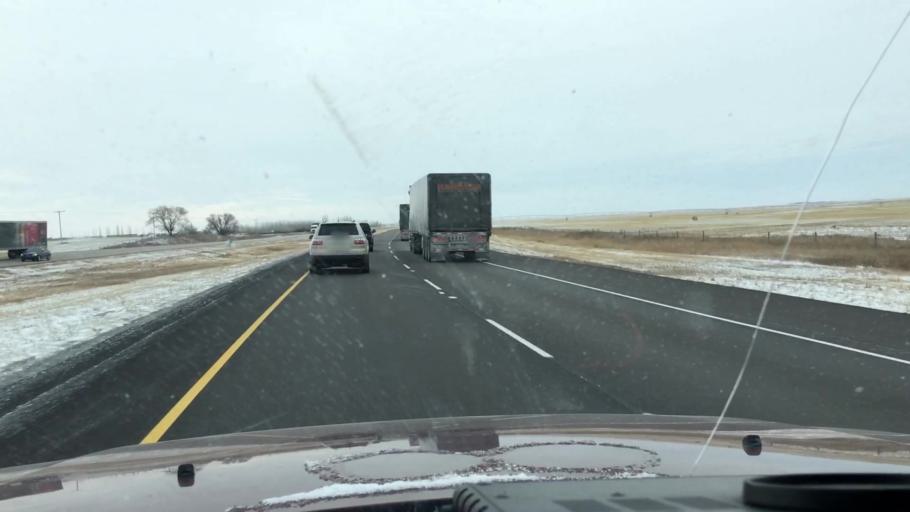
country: CA
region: Saskatchewan
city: Saskatoon
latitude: 51.7784
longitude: -106.4765
